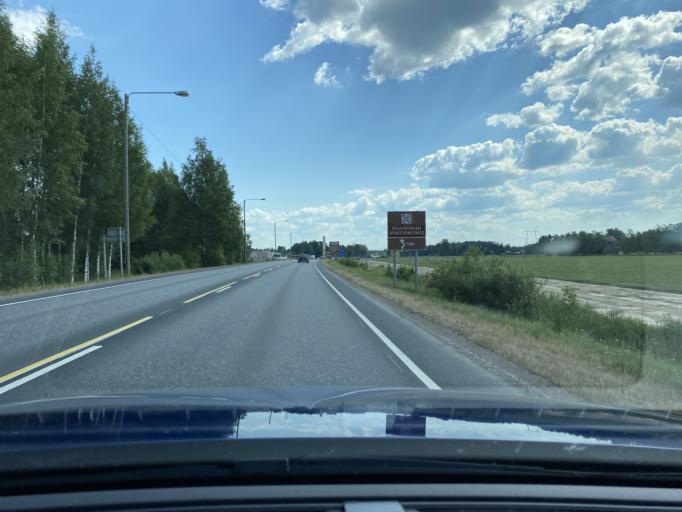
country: FI
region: Satakunta
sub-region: Rauma
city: Eura
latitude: 61.1356
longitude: 22.1210
